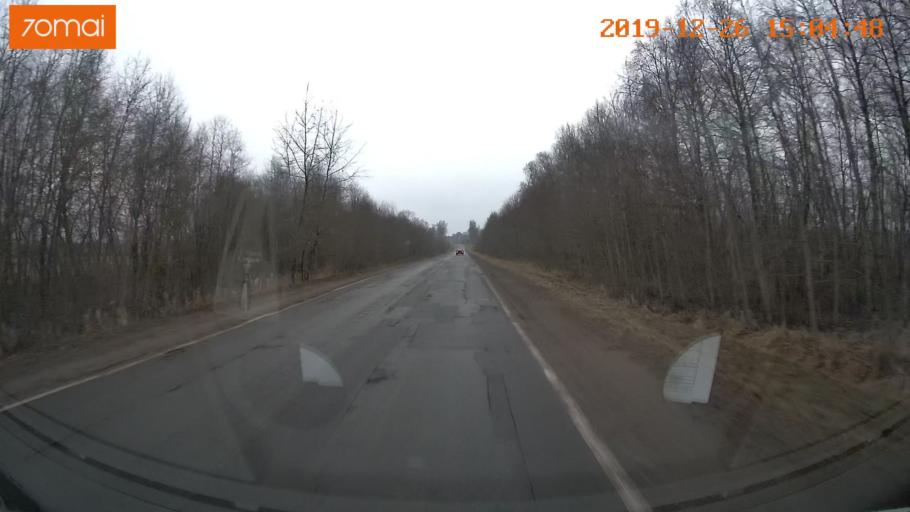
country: RU
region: Jaroslavl
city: Rybinsk
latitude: 58.1959
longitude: 38.8579
